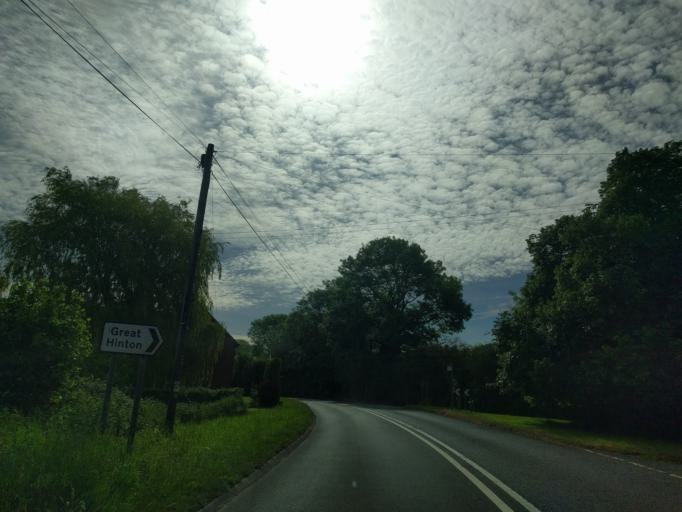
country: GB
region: England
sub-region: Wiltshire
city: Seend
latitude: 51.3367
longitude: -2.1205
